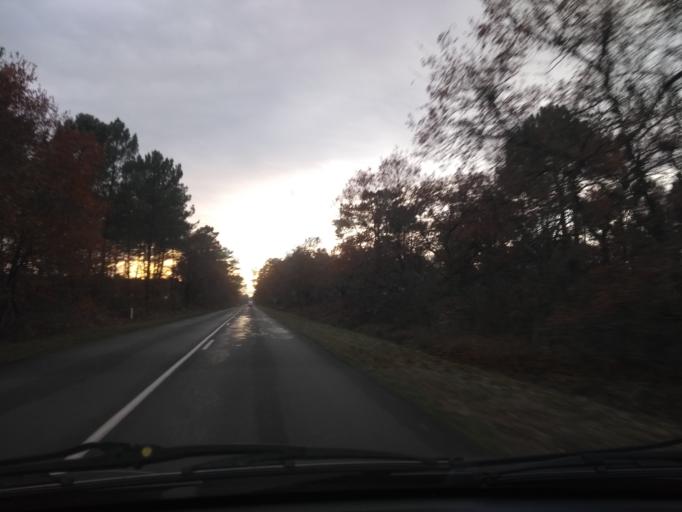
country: FR
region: Aquitaine
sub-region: Departement de la Gironde
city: Saucats
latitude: 44.6435
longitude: -0.6310
